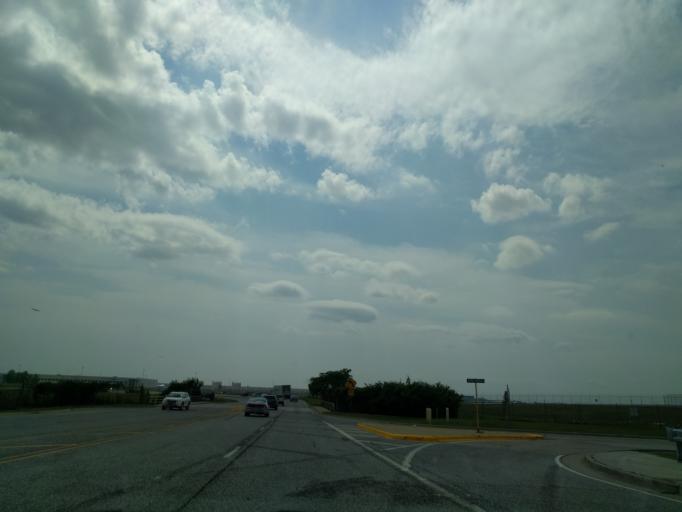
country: US
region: Illinois
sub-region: Cook County
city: Rosemont
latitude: 42.0026
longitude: -87.8942
